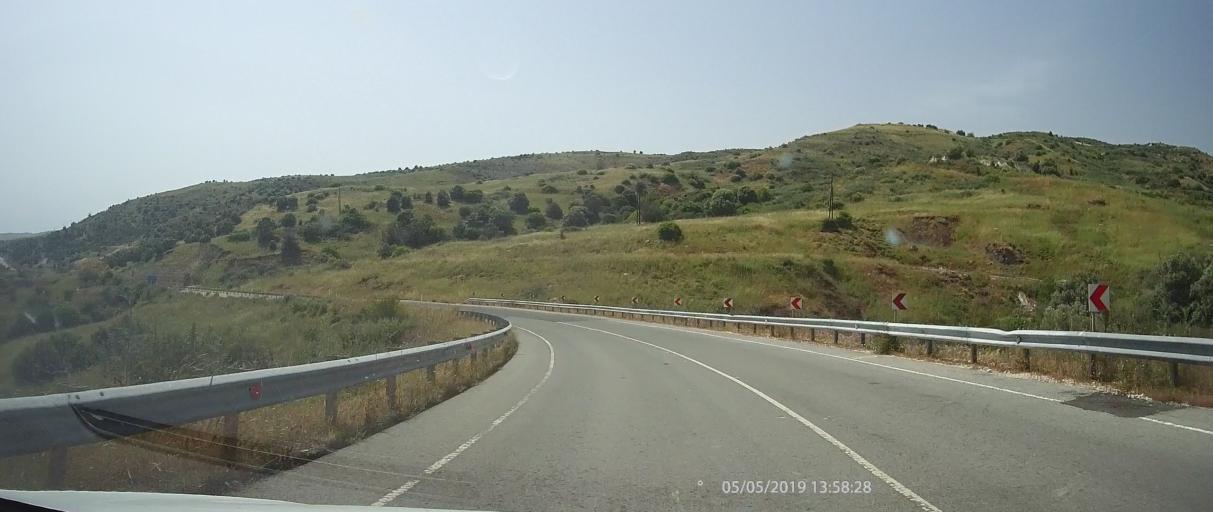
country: CY
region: Limassol
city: Pachna
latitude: 34.7898
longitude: 32.6900
